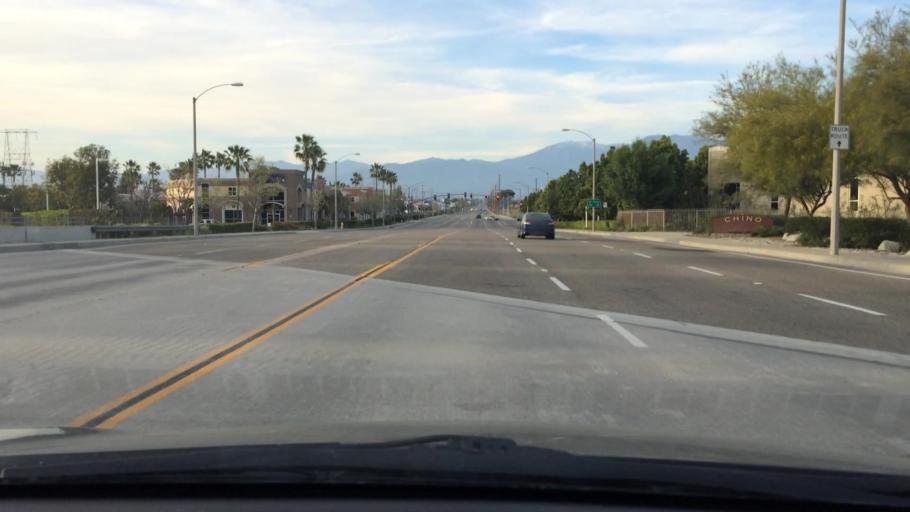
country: US
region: California
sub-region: San Bernardino County
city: Los Serranos
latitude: 33.9741
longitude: -117.6889
